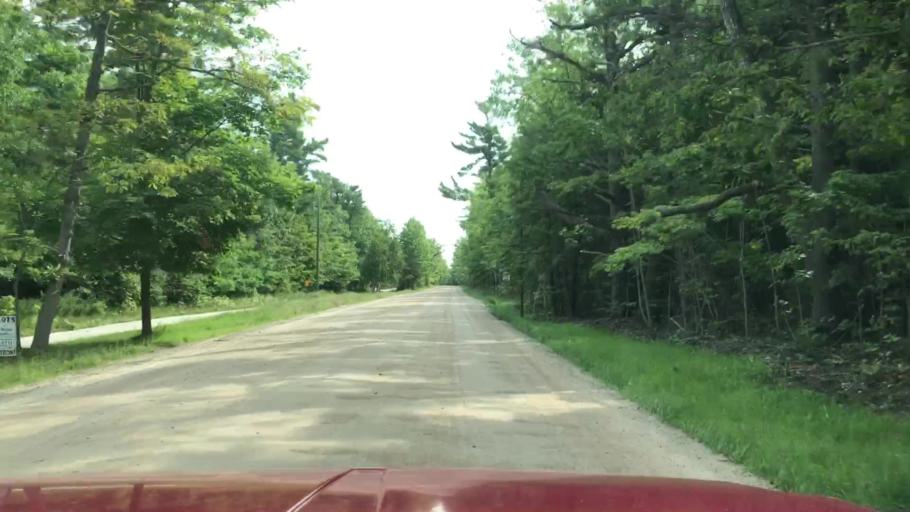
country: US
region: Michigan
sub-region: Charlevoix County
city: Charlevoix
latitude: 45.7468
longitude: -85.5324
